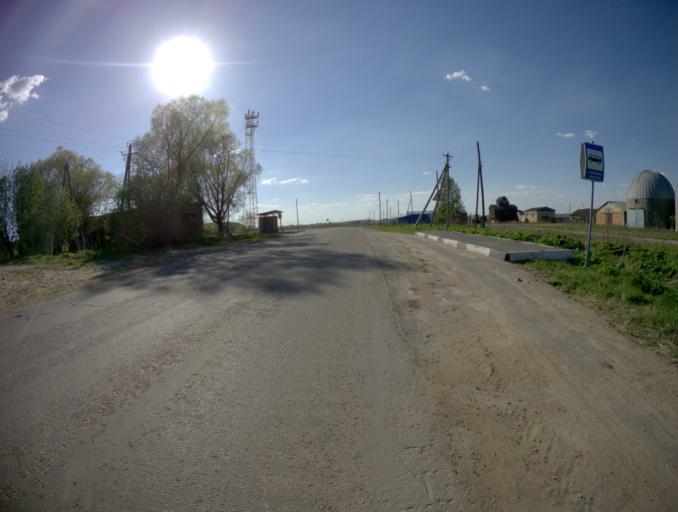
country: RU
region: Ivanovo
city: Gavrilov Posad
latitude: 56.3454
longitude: 40.1856
